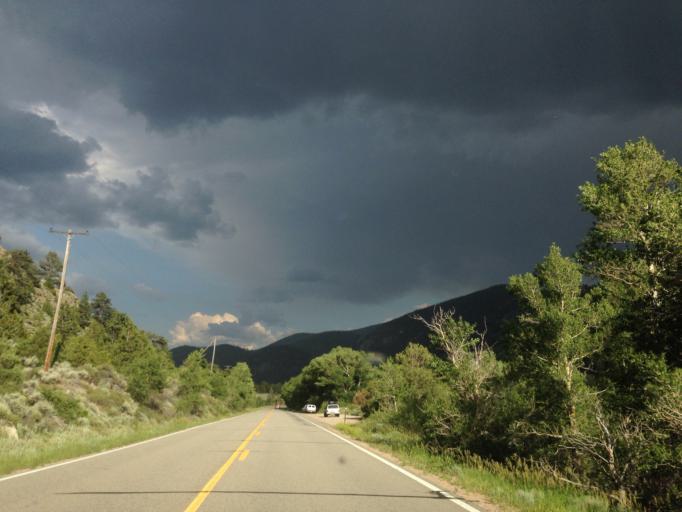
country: US
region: Colorado
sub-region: Larimer County
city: Estes Park
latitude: 40.6993
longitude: -105.7003
